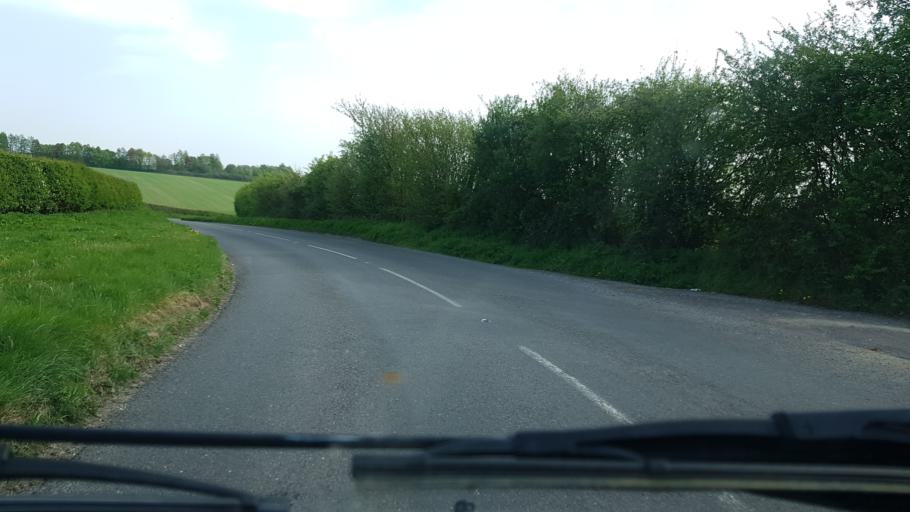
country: GB
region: England
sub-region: Hampshire
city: Overton
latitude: 51.2601
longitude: -1.2645
